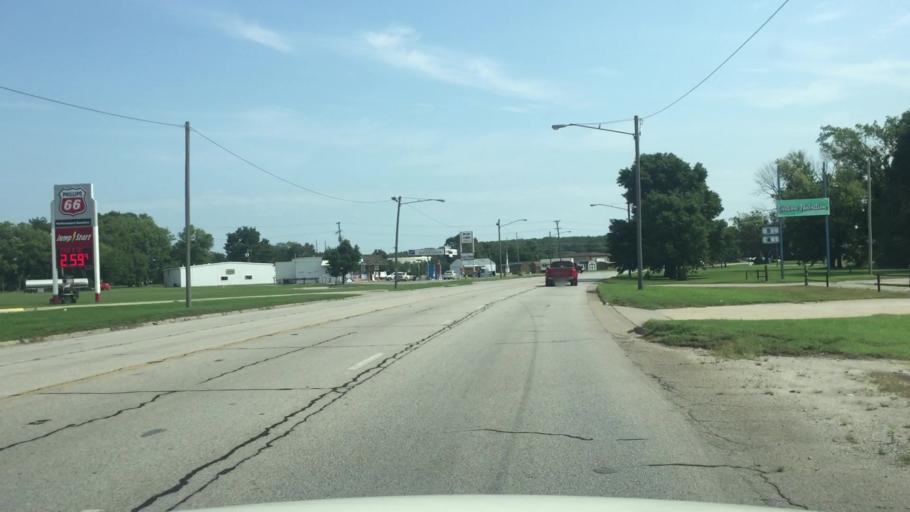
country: US
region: Kansas
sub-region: Montgomery County
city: Coffeyville
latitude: 37.0380
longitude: -95.5986
